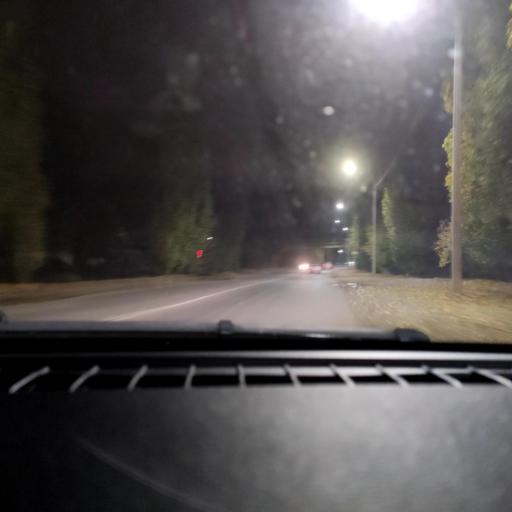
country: RU
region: Voronezj
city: Maslovka
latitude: 51.6231
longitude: 39.2611
